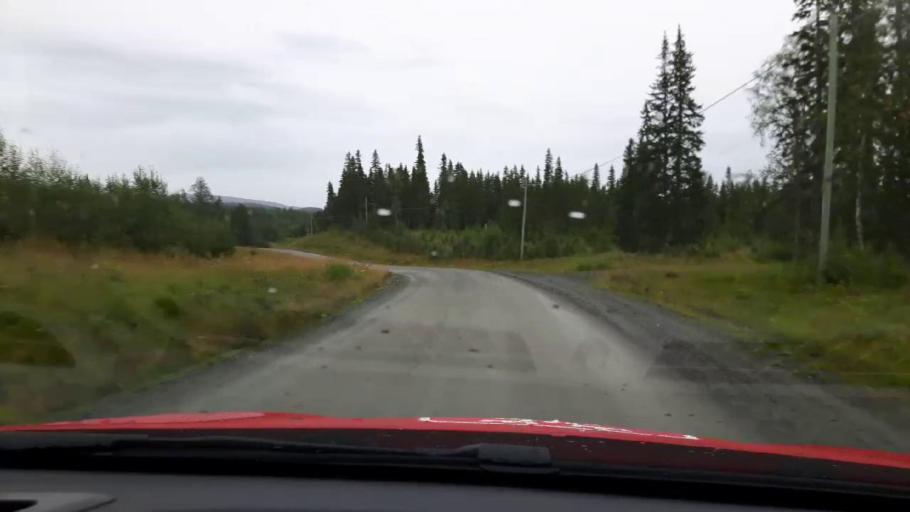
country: SE
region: Jaemtland
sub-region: Are Kommun
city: Are
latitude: 63.4972
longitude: 12.7604
